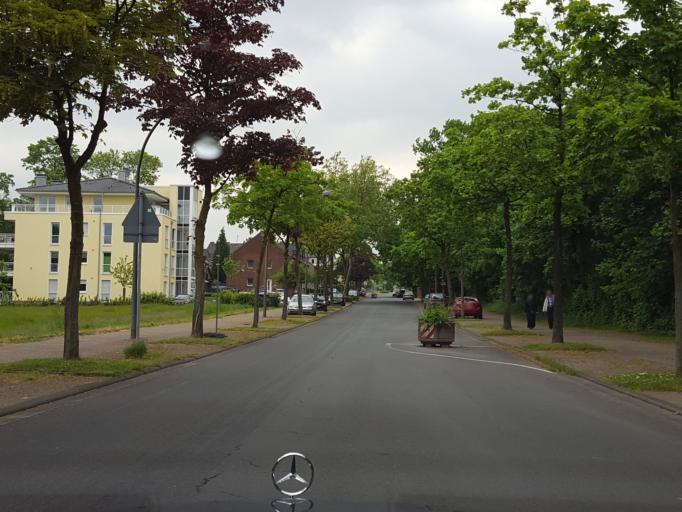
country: DE
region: North Rhine-Westphalia
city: Oer-Erkenschwick
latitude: 51.6370
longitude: 7.2671
